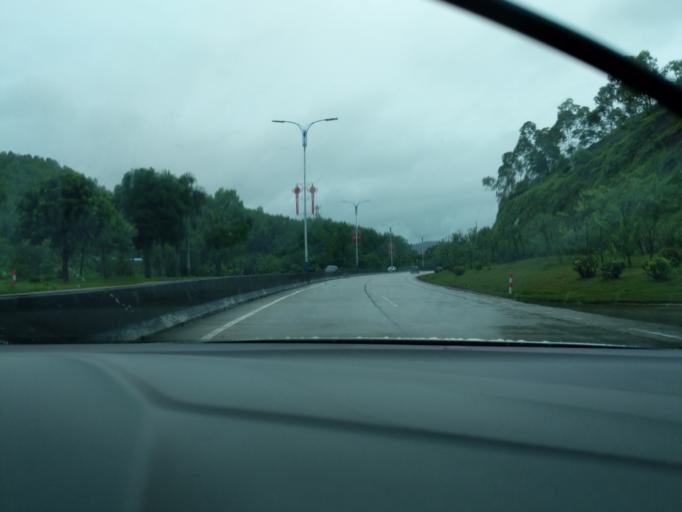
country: CN
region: Guangdong
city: Pingshi
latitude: 22.2287
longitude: 112.3115
